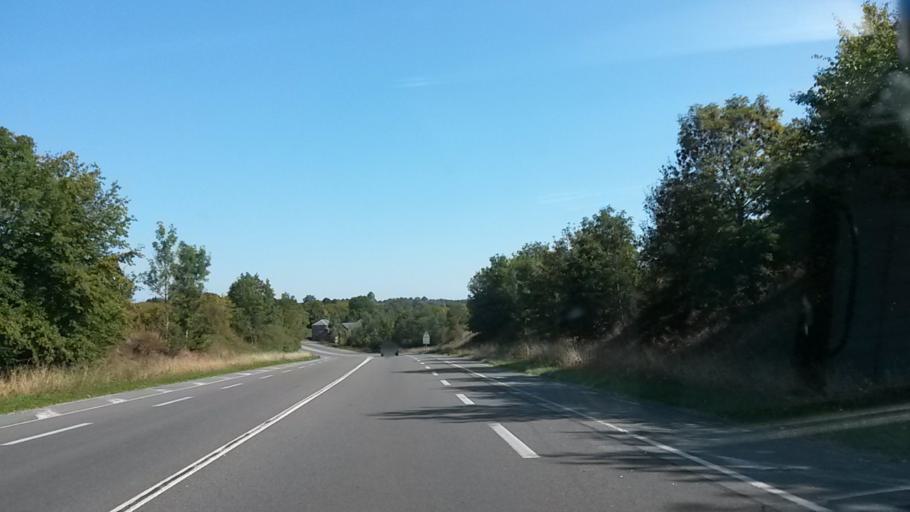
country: FR
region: Nord-Pas-de-Calais
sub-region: Departement du Nord
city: Avesnelles
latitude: 50.1357
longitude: 3.9449
